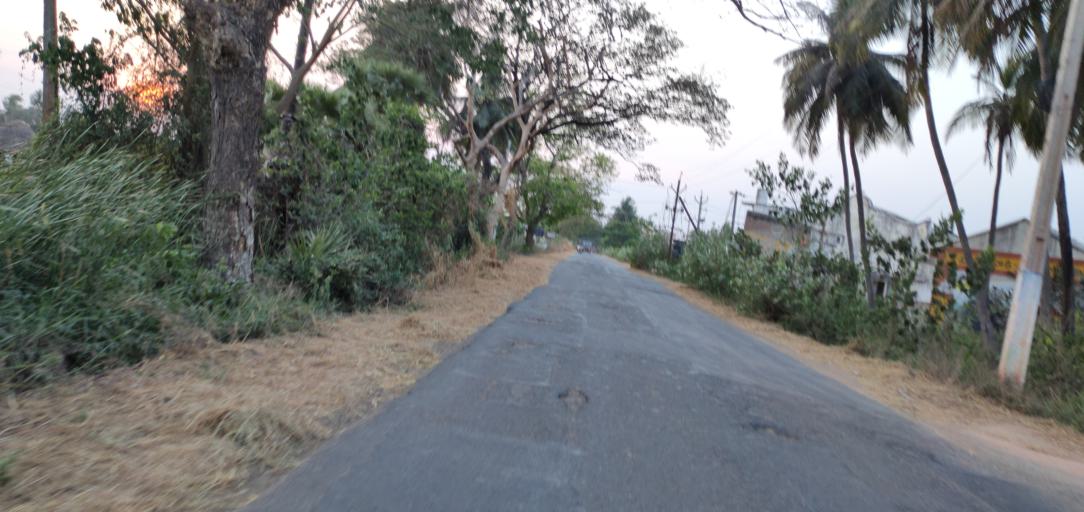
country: IN
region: Andhra Pradesh
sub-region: West Godavari
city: Tadepallegudem
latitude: 16.8497
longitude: 81.4882
